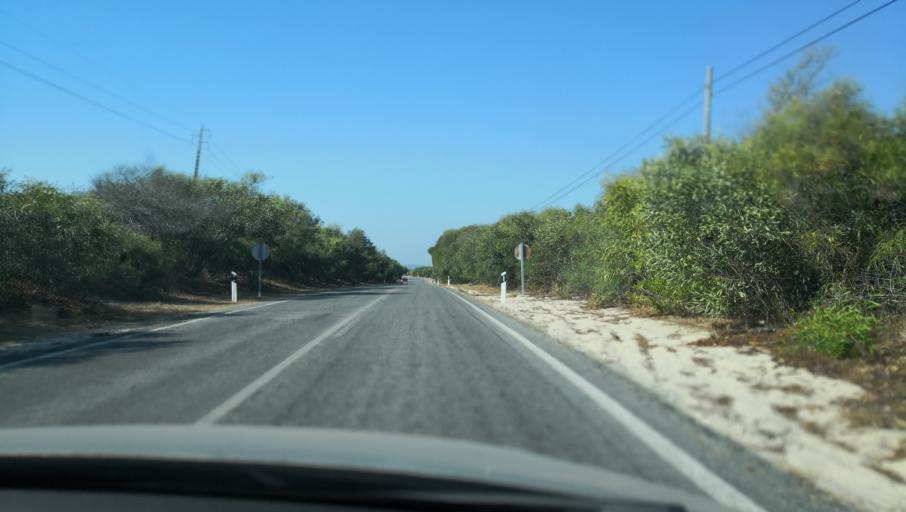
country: PT
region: Setubal
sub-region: Setubal
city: Setubal
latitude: 38.4139
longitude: -8.8150
